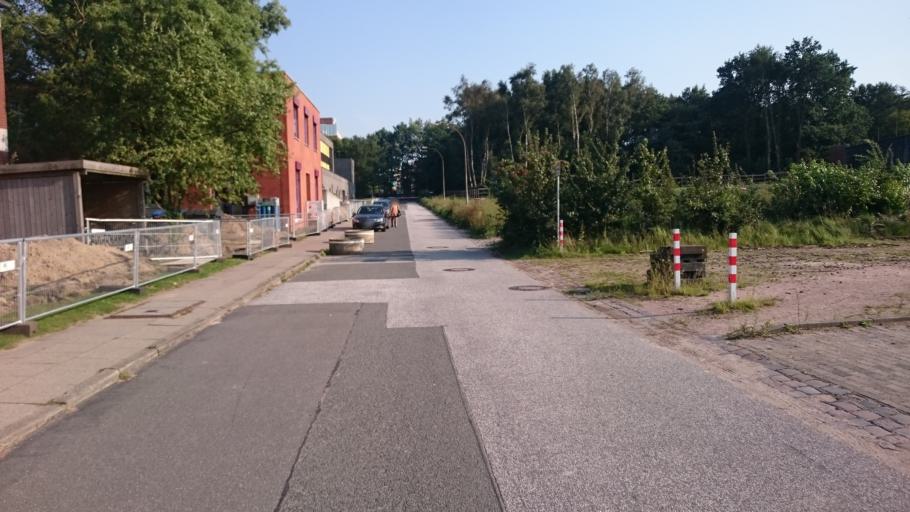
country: DE
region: Hamburg
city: Eidelstedt
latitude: 53.5780
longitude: 9.8855
